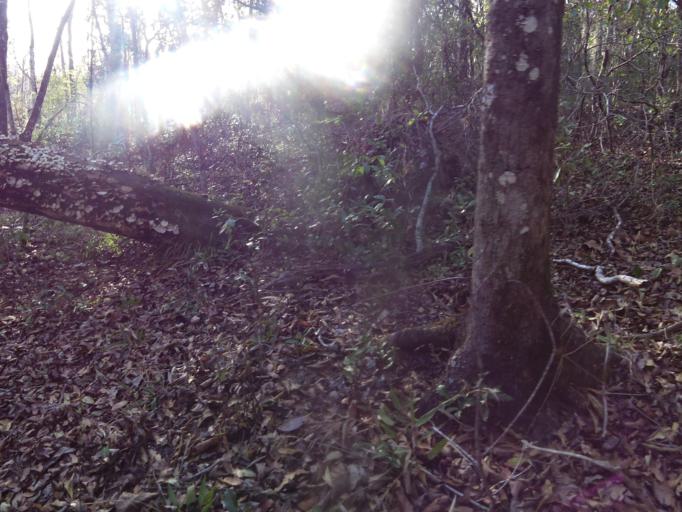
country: US
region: Florida
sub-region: Clay County
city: Middleburg
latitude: 30.1483
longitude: -81.9547
